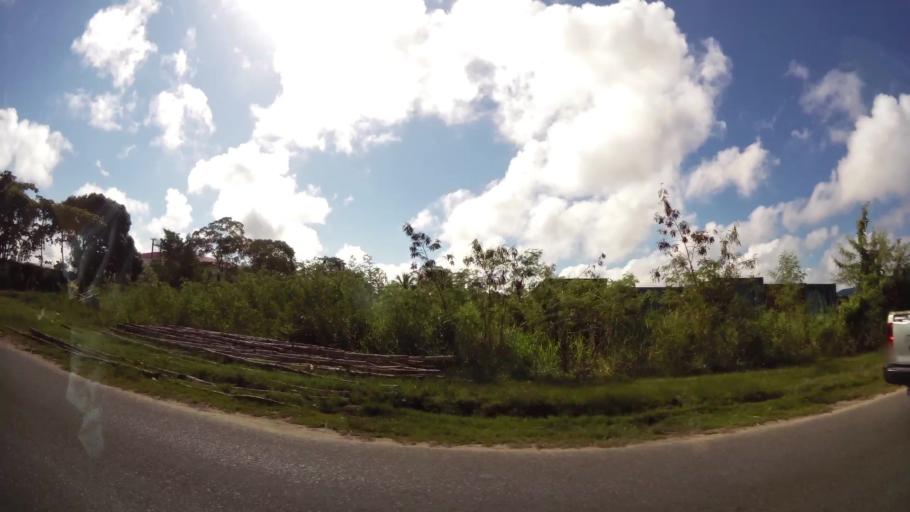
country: SR
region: Commewijne
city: Nieuw Amsterdam
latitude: 5.8622
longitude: -55.1018
